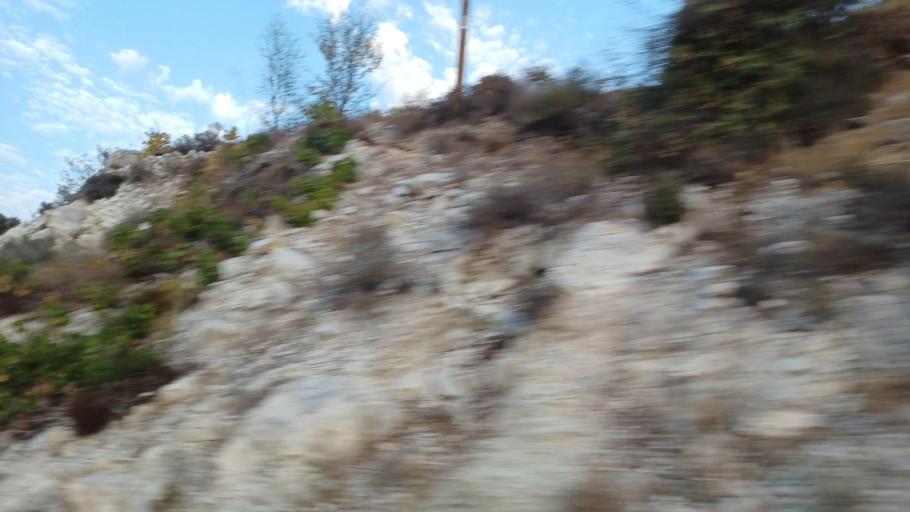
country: CY
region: Limassol
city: Pelendri
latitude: 34.8075
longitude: 32.9619
